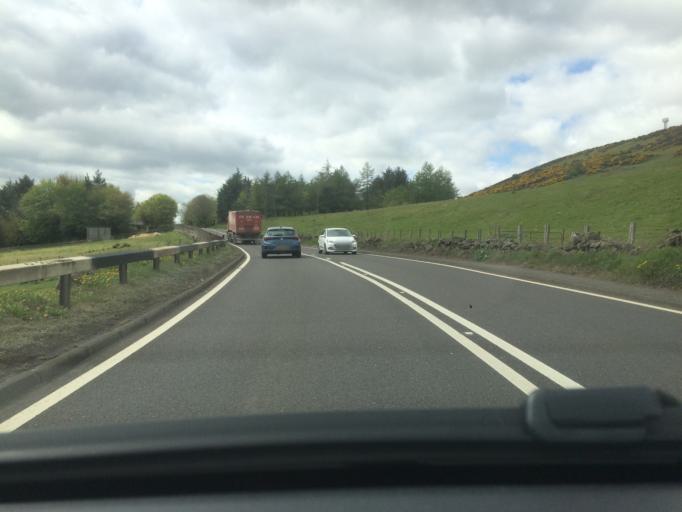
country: GB
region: Scotland
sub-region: Midlothian
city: Penicuik
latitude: 55.8458
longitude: -3.2373
